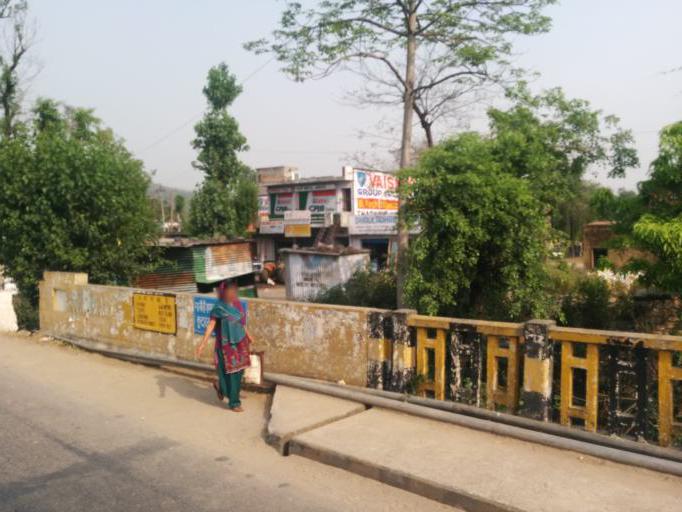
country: IN
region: Punjab
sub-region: Gurdaspur
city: Dharkalan
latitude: 32.2831
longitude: 75.8531
